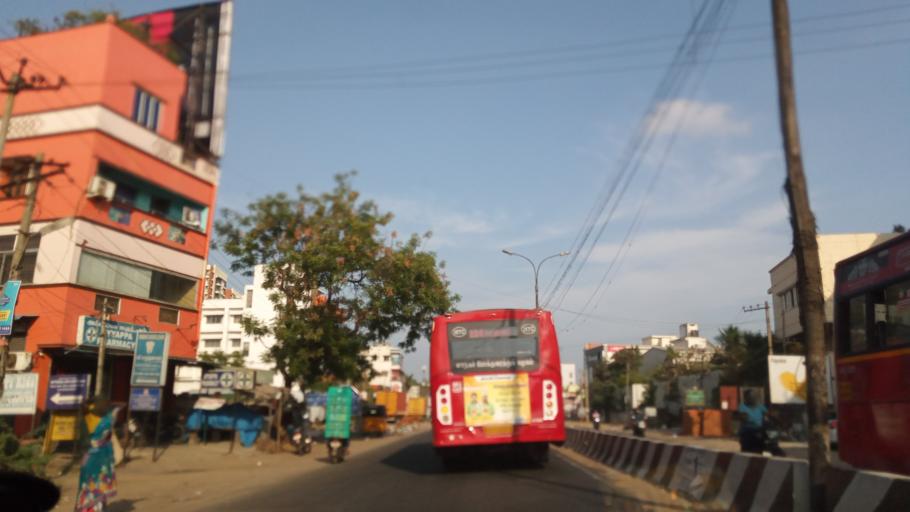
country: IN
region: Tamil Nadu
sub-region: Kancheepuram
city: Poonamalle
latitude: 13.0403
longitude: 80.1295
